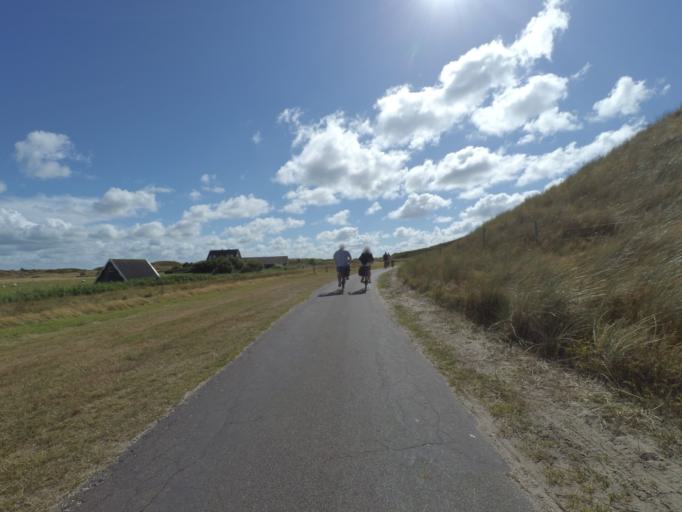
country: NL
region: North Holland
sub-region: Gemeente Texel
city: Den Burg
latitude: 53.1126
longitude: 4.7950
